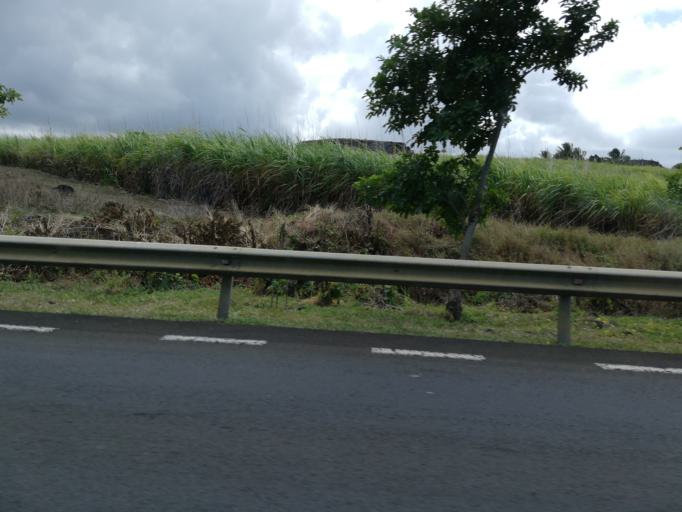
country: MU
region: Grand Port
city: Plaine Magnien
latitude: -20.4335
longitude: 57.6371
